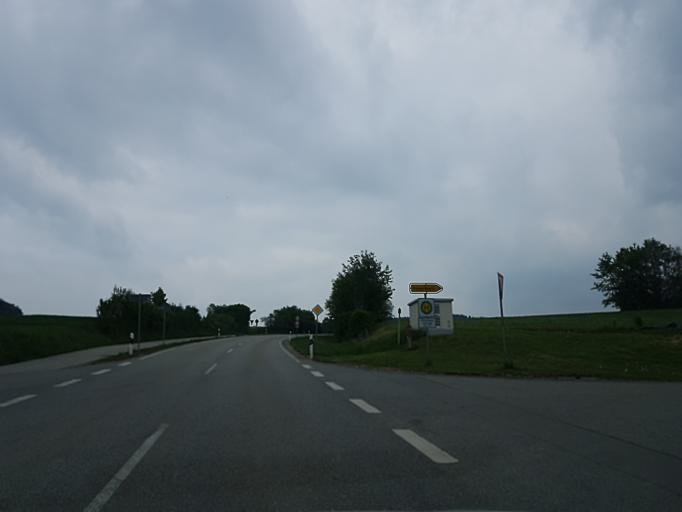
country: DE
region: Bavaria
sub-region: Upper Bavaria
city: Ebersberg
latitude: 48.0908
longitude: 11.9727
